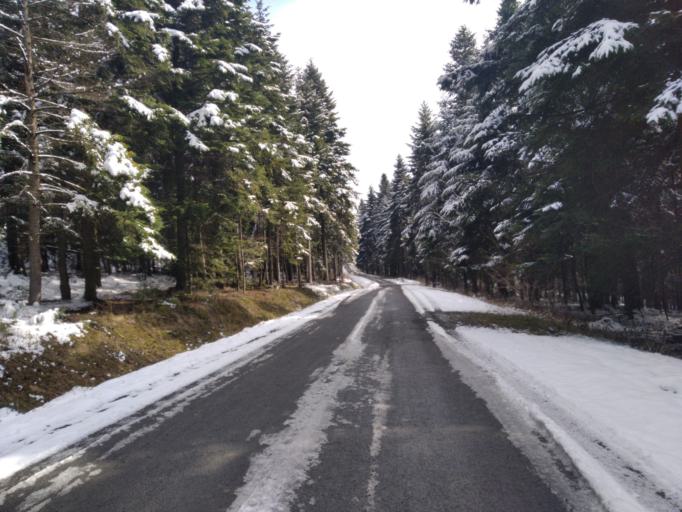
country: PL
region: Subcarpathian Voivodeship
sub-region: Powiat ropczycko-sedziszowski
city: Ropczyce
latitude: 50.0156
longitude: 21.6035
